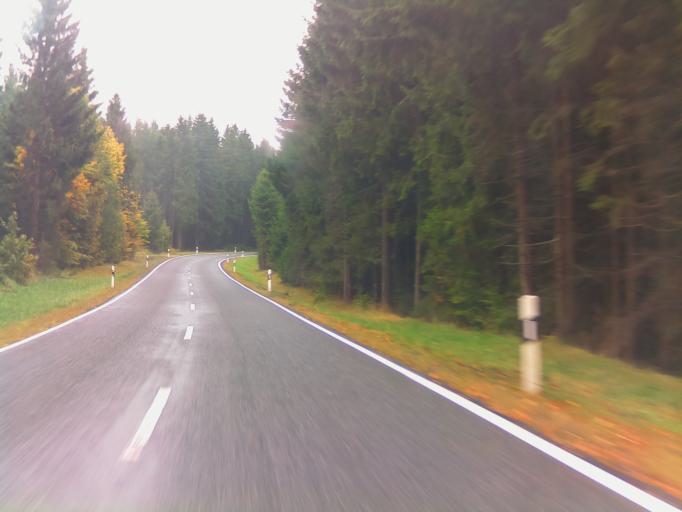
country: DE
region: Bavaria
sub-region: Upper Franconia
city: Tschirn
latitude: 50.4200
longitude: 11.4545
